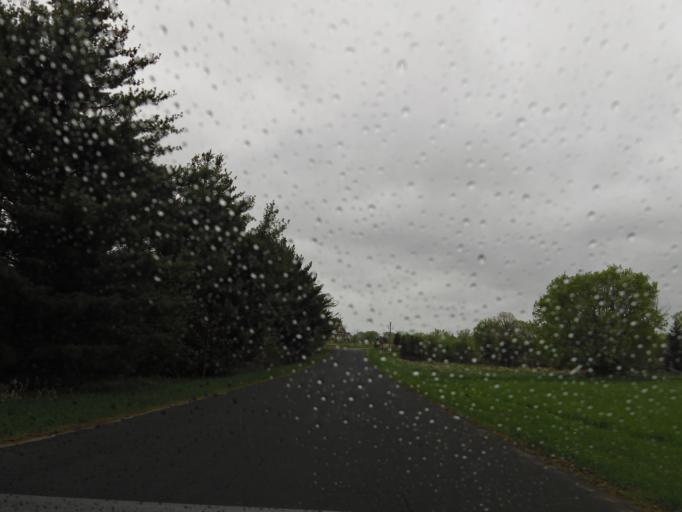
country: US
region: Minnesota
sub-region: Washington County
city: Lake Elmo
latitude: 44.9914
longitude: -92.8354
